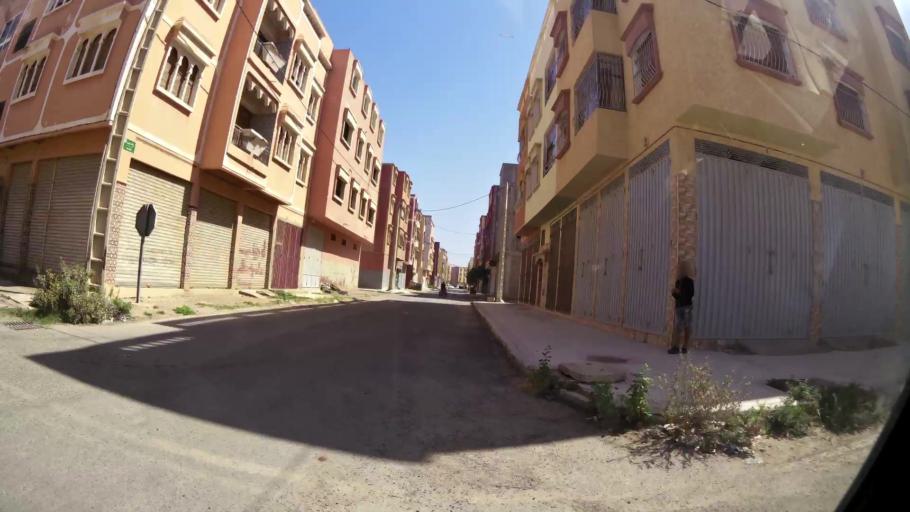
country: MA
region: Souss-Massa-Draa
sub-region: Inezgane-Ait Mellou
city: Inezgane
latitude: 30.3298
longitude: -9.5073
